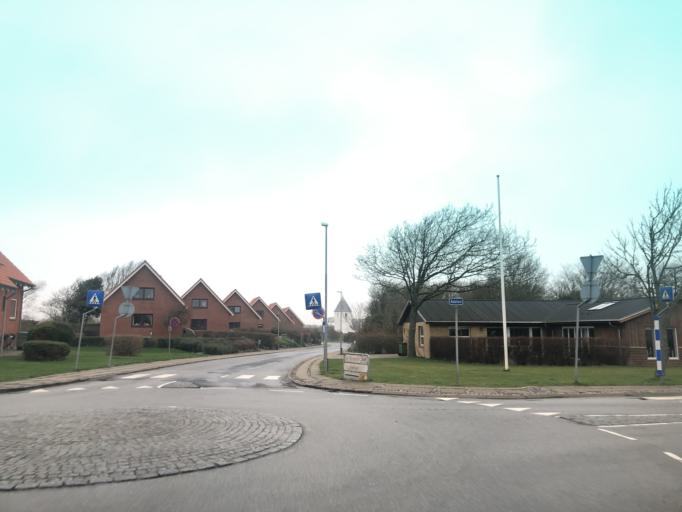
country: DK
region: North Denmark
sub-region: Thisted Kommune
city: Hurup
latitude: 56.7518
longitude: 8.4239
